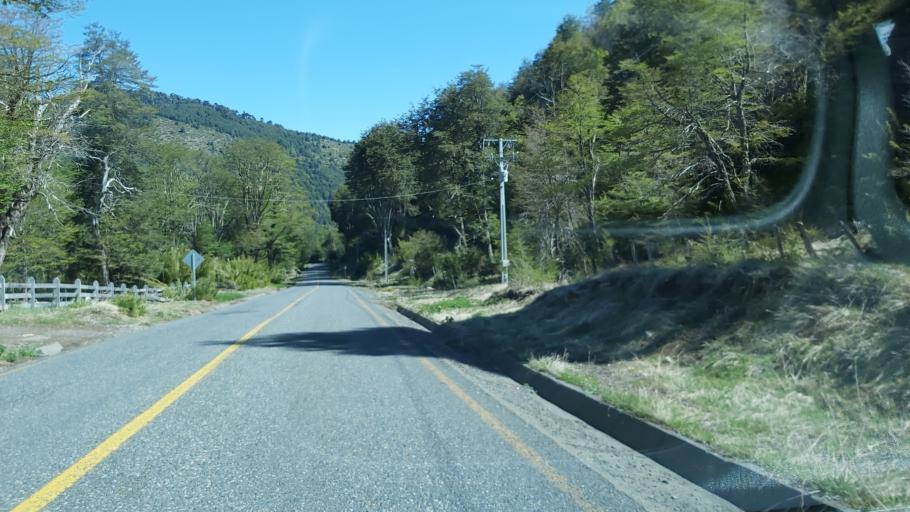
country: CL
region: Araucania
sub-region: Provincia de Cautin
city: Vilcun
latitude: -38.4575
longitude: -71.5160
